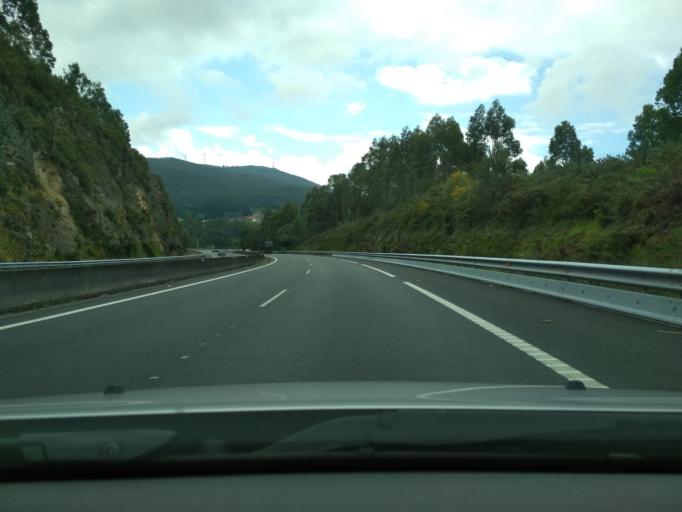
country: ES
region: Galicia
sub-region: Provincia da Coruna
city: Padron
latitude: 42.7819
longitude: -8.6444
